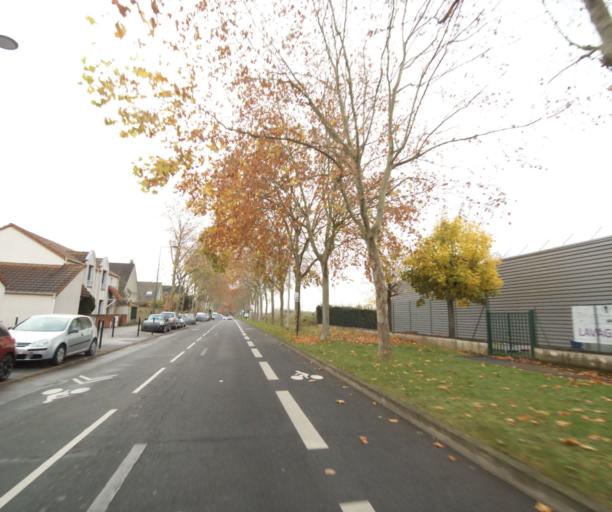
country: FR
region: Ile-de-France
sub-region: Departement de l'Essonne
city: Lisses
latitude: 48.6165
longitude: 2.4316
